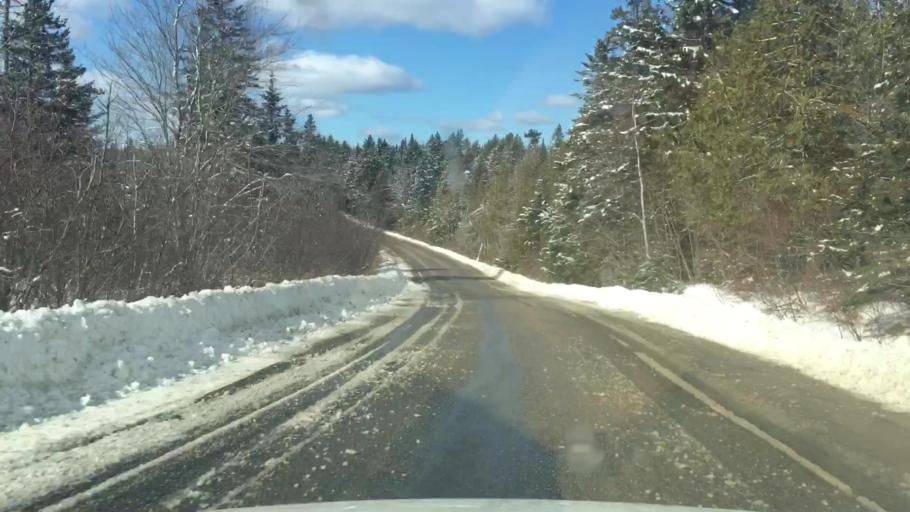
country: US
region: Maine
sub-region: Washington County
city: Machias
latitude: 44.6829
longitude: -67.4568
